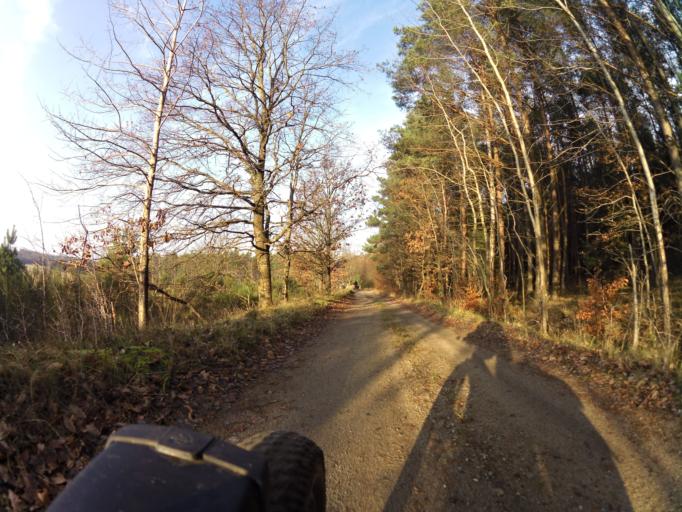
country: PL
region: West Pomeranian Voivodeship
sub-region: Powiat koszalinski
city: Polanow
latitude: 54.0987
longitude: 16.6483
